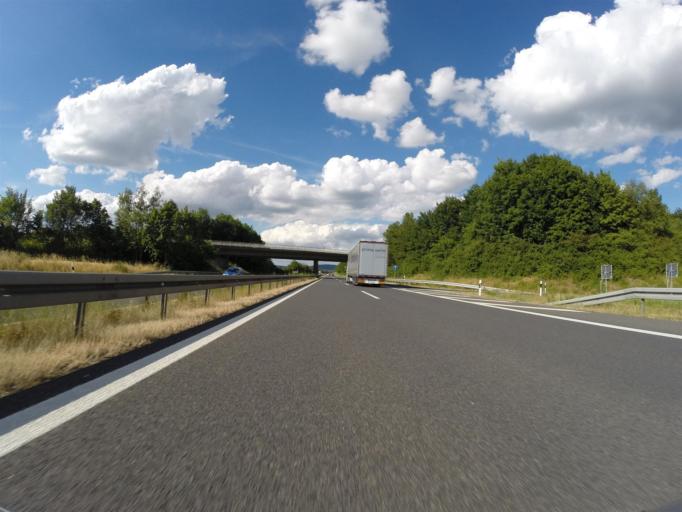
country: DE
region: Bavaria
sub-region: Upper Franconia
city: Bad Staffelstein
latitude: 50.1085
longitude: 11.0137
